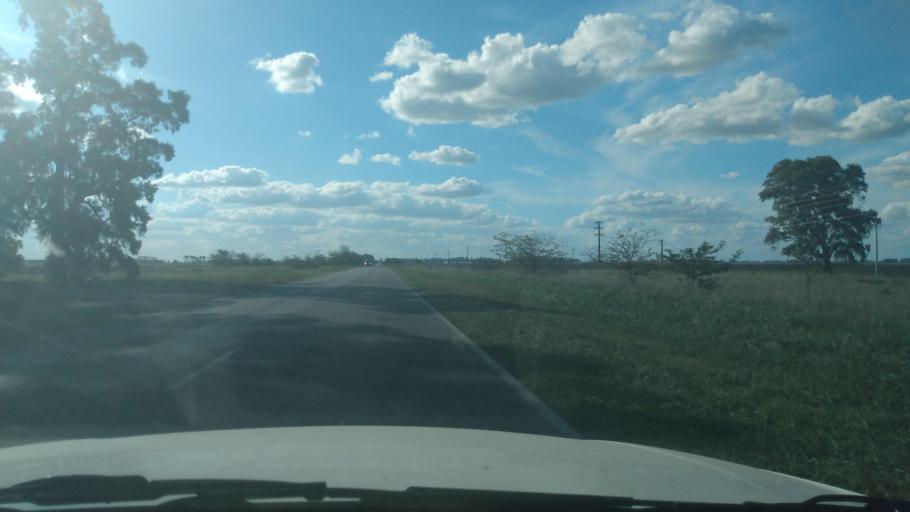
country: AR
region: Buenos Aires
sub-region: Partido de Navarro
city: Navarro
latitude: -34.9227
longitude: -59.3272
